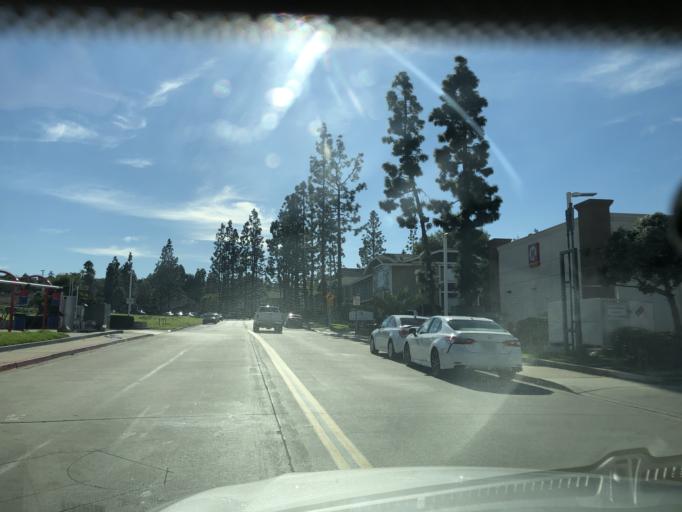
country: US
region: California
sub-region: San Diego County
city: Chula Vista
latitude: 32.6478
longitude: -117.0642
